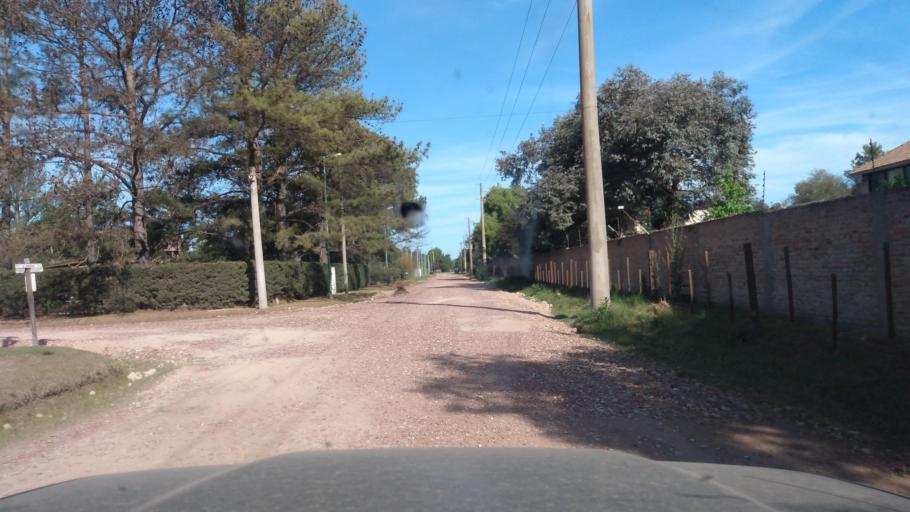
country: AR
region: Buenos Aires
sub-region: Partido de Lujan
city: Lujan
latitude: -34.5942
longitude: -59.1441
